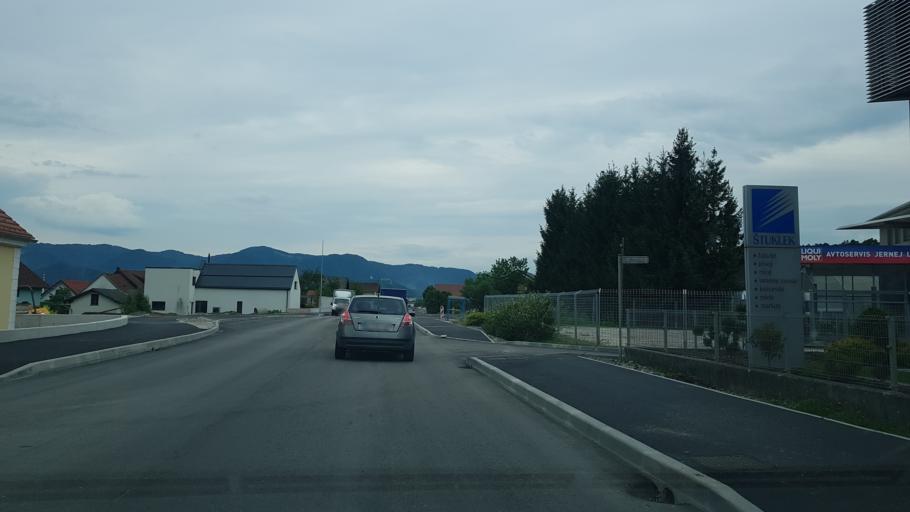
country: SI
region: Celje
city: Trnovlje pri Celju
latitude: 46.2643
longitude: 15.2833
